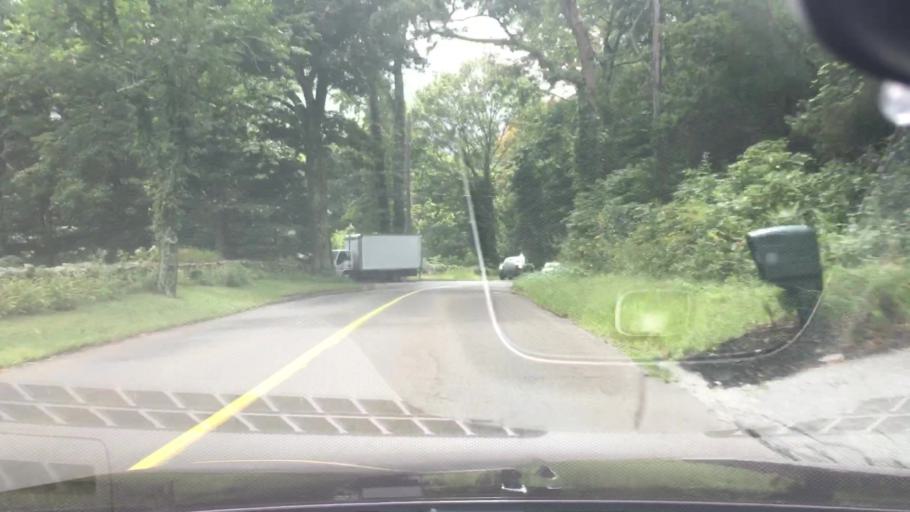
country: US
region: Connecticut
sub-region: New Haven County
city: Madison
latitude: 41.3477
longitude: -72.5628
